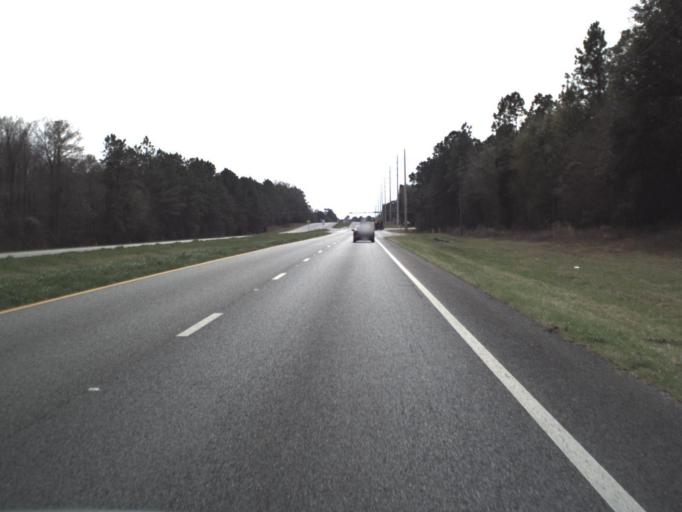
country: US
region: Florida
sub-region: Washington County
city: Chipley
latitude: 30.7370
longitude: -85.3861
